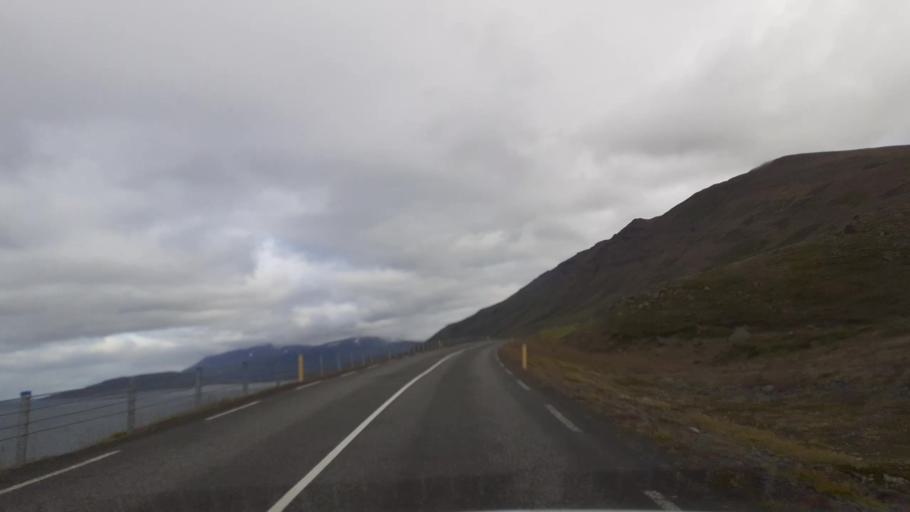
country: IS
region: Northeast
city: Akureyri
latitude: 65.8282
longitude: -18.0582
